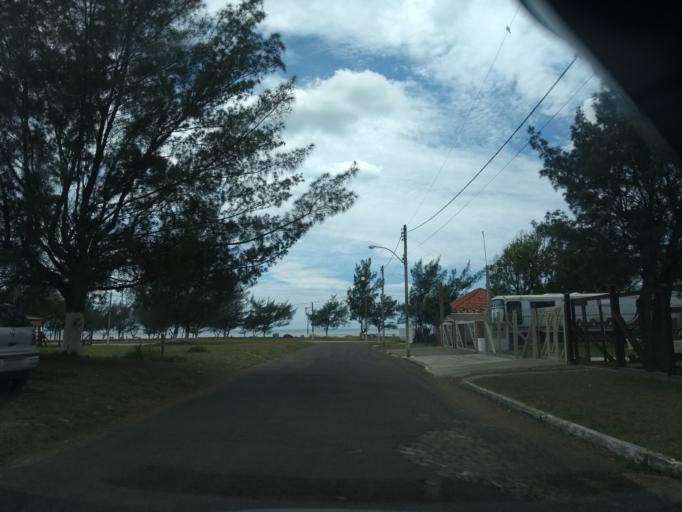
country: BR
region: Rio Grande do Sul
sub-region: Tramandai
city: Tramandai
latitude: -30.0632
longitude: -50.1603
